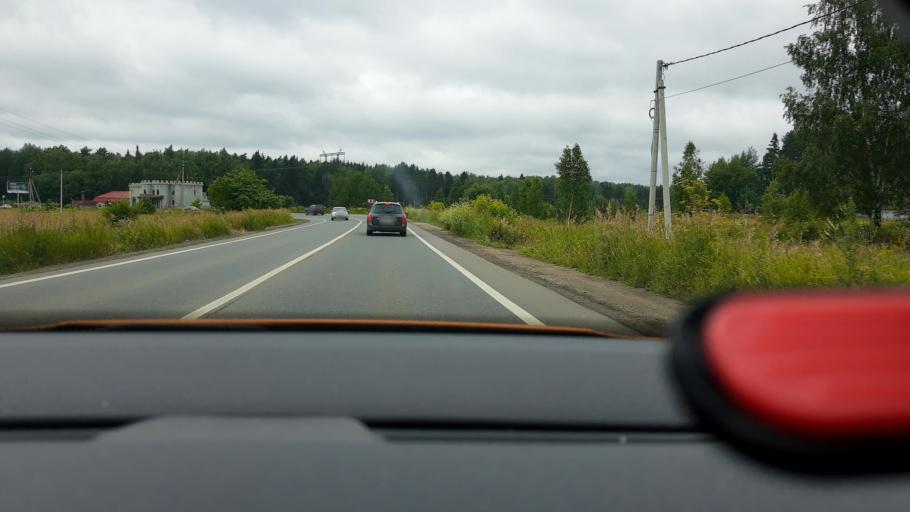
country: RU
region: Moskovskaya
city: Pirogovskiy
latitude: 55.9993
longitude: 37.7045
